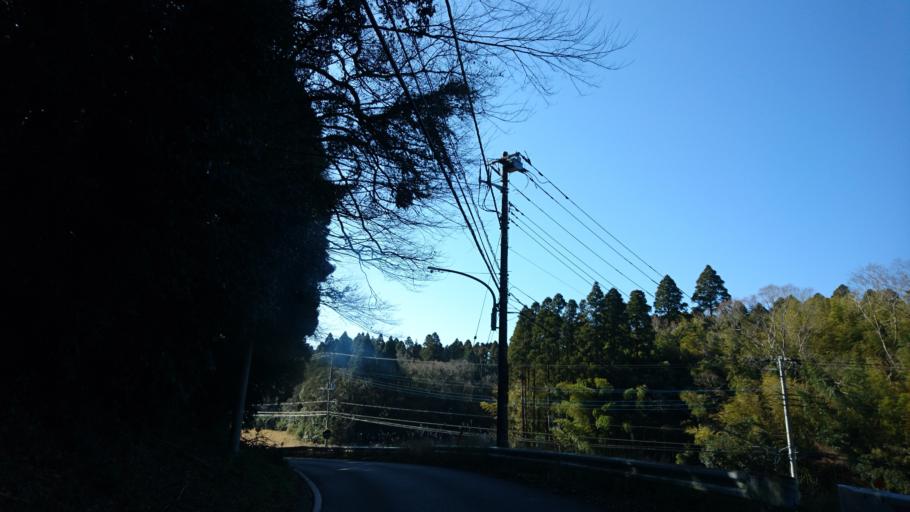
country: JP
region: Chiba
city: Yachimata
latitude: 35.6120
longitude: 140.3464
